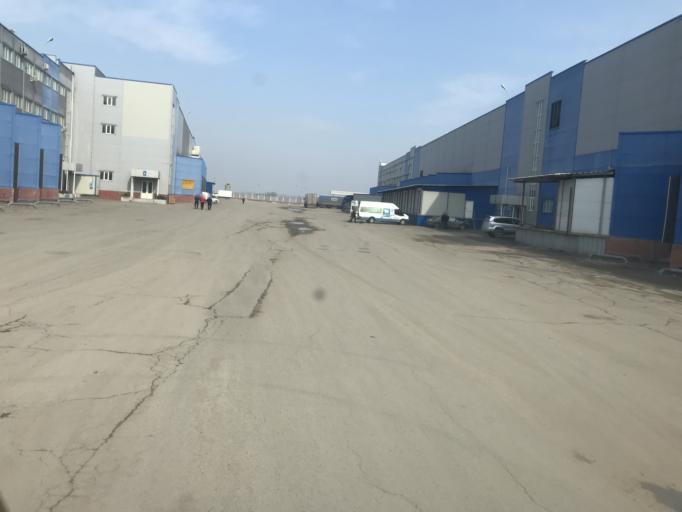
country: KZ
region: Almaty Oblysy
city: Pervomayskiy
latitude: 43.3622
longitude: 76.9764
